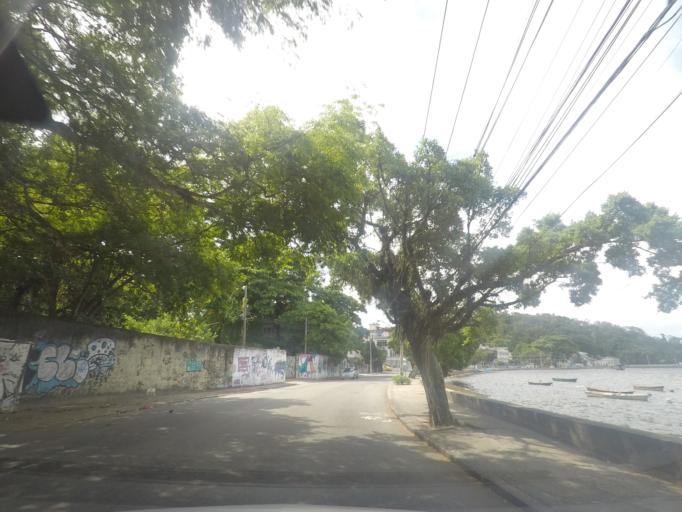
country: BR
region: Rio de Janeiro
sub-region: Rio De Janeiro
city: Rio de Janeiro
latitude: -22.8174
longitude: -43.1758
